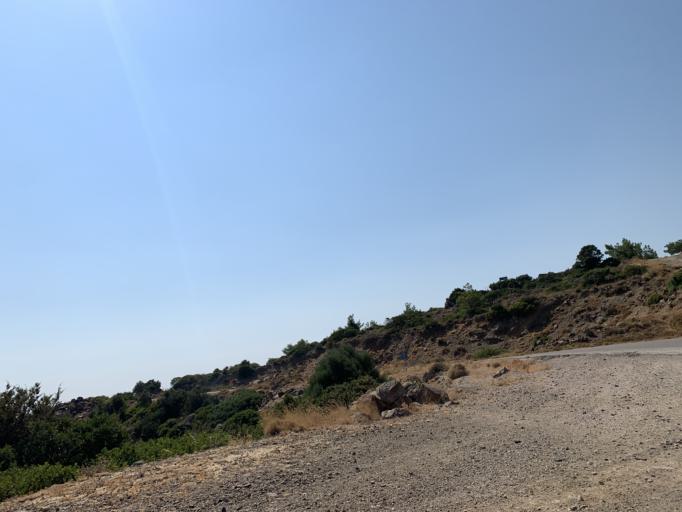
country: GR
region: North Aegean
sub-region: Chios
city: Thymiana
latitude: 38.2231
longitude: 25.9404
